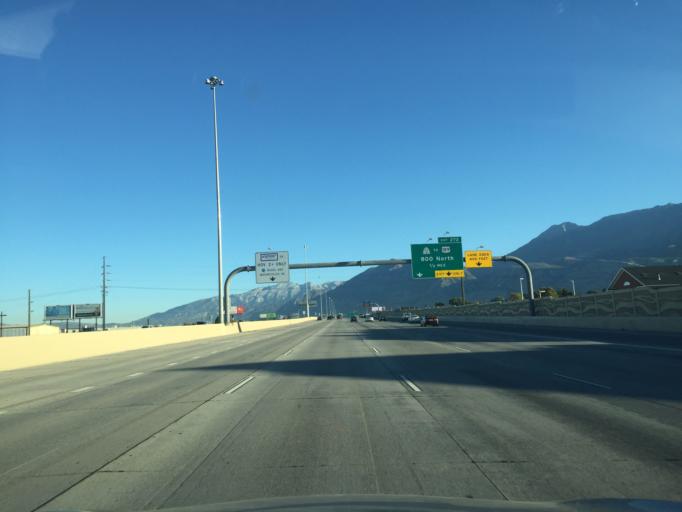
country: US
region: Utah
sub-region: Utah County
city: Orem
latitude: 40.3012
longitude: -111.7257
